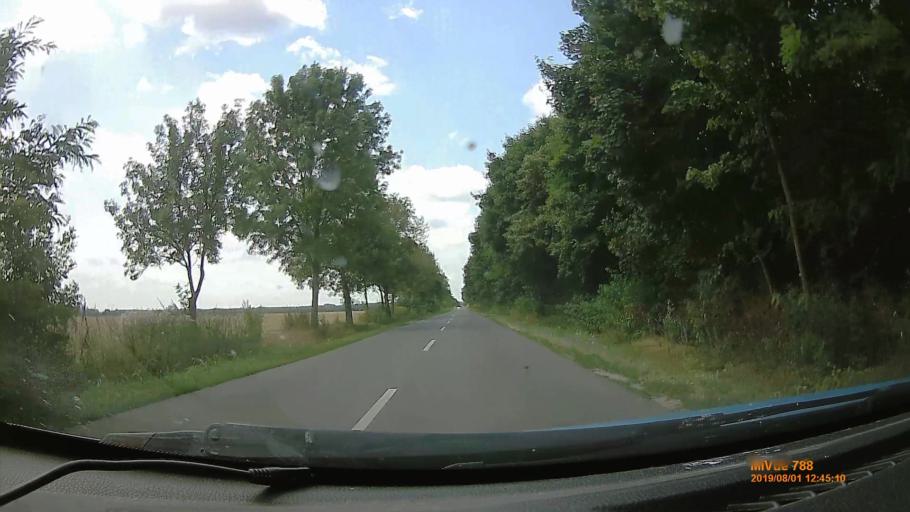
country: HR
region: Osjecko-Baranjska
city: Viljevo
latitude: 45.8347
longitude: 18.1269
